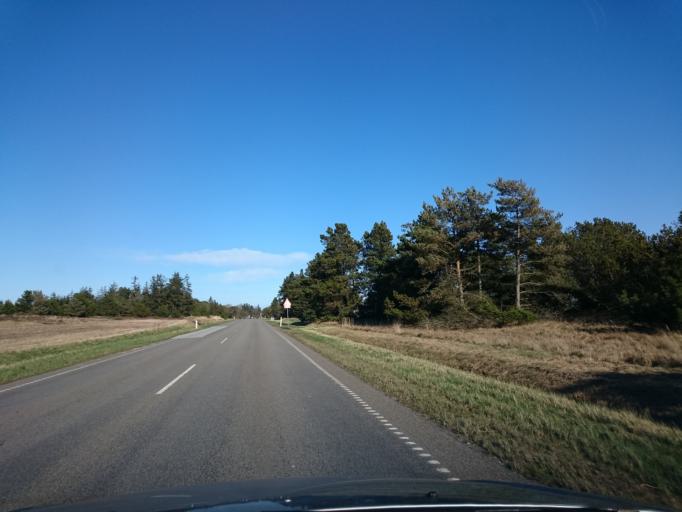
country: DK
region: North Denmark
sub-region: Frederikshavn Kommune
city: Strandby
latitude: 57.6058
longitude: 10.3827
